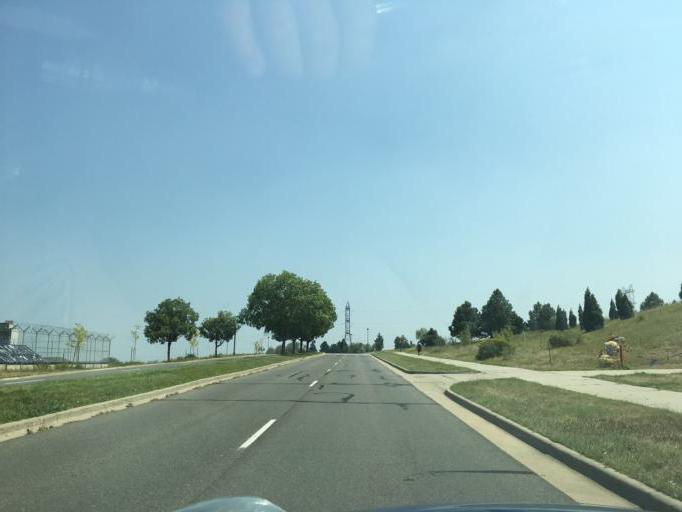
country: US
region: Colorado
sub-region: Jefferson County
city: West Pleasant View
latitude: 39.7297
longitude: -105.2024
